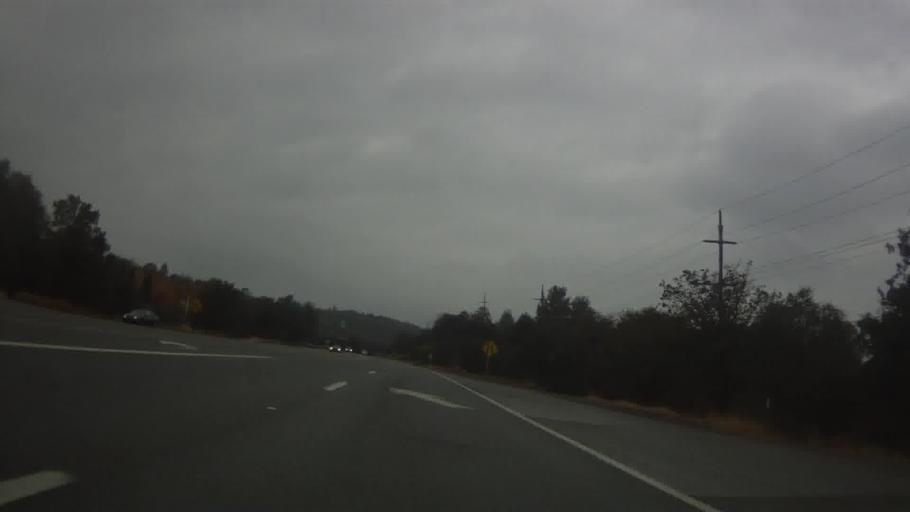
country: US
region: California
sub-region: Shasta County
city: Redding
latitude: 40.5834
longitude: -122.4288
